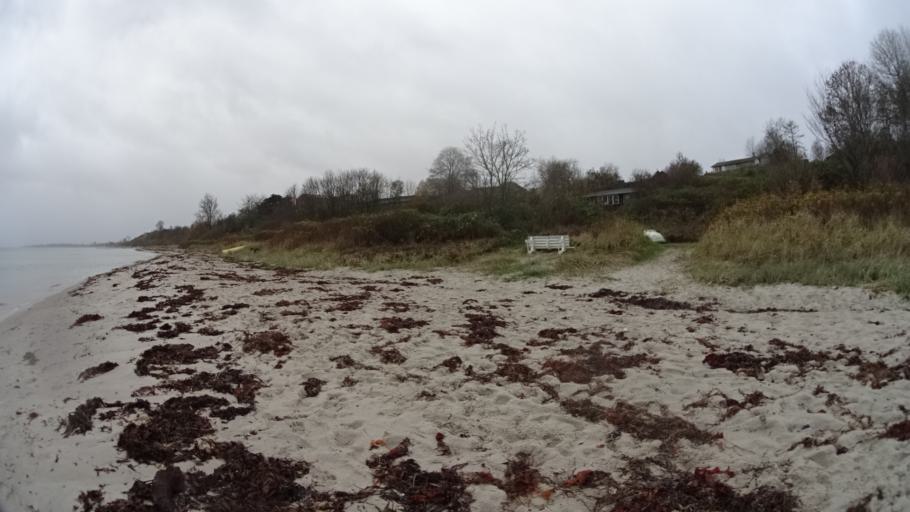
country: DK
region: Central Jutland
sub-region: Arhus Kommune
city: Malling
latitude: 55.9928
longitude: 10.2535
